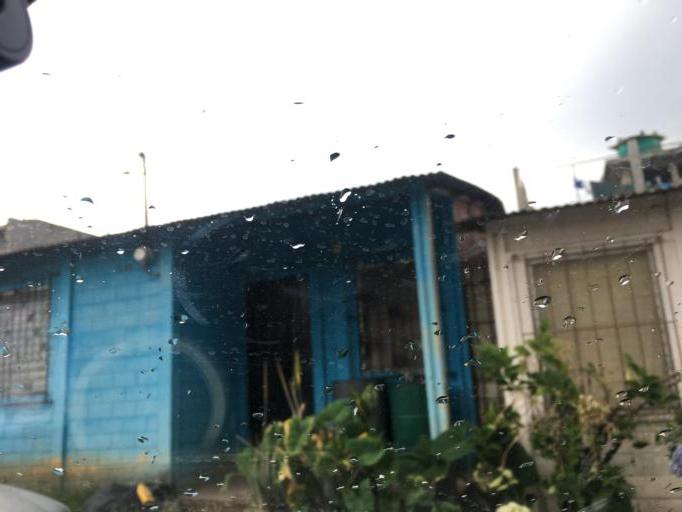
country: GT
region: Guatemala
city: Petapa
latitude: 14.5050
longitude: -90.5523
